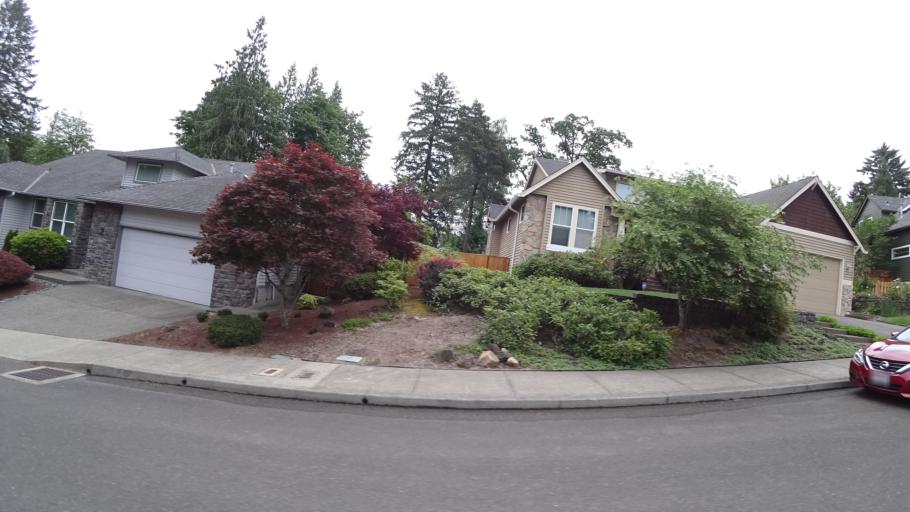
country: US
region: Oregon
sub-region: Washington County
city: Garden Home-Whitford
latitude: 45.4689
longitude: -122.7415
